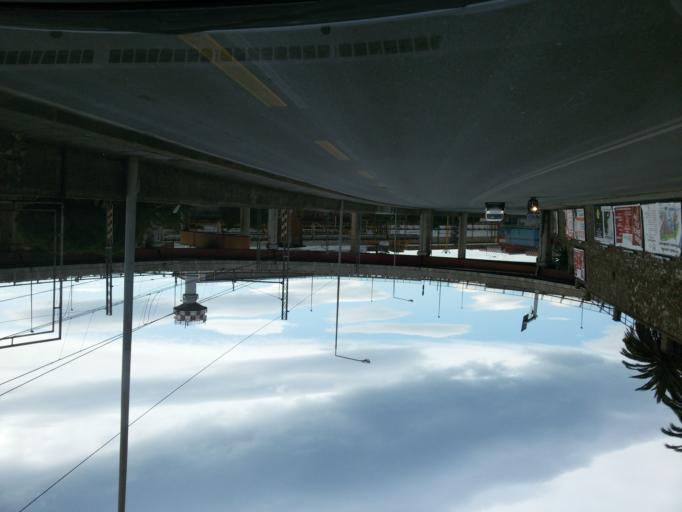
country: IT
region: Liguria
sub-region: Provincia di Genova
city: San Teodoro
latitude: 44.4170
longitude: 8.8598
